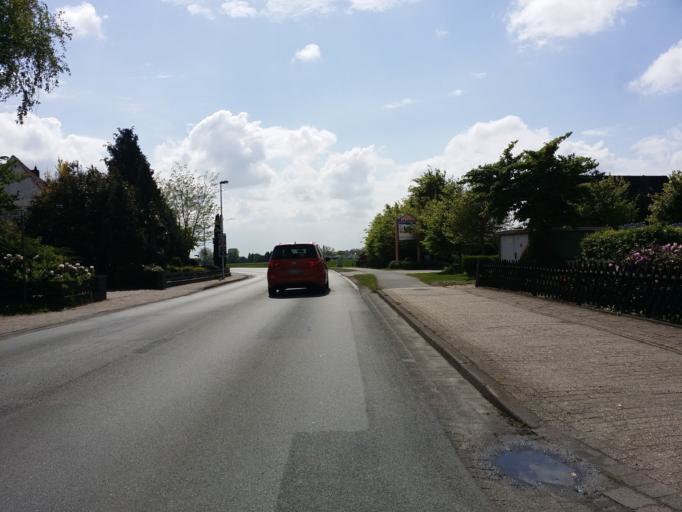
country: DE
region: Lower Saxony
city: Stuhr
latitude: 53.0248
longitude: 8.7445
